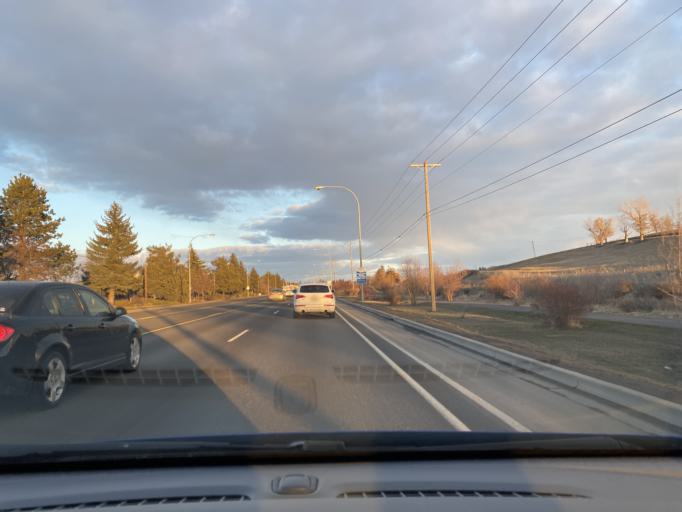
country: US
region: Idaho
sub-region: Latah County
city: Moscow
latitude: 46.7325
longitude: -117.0312
